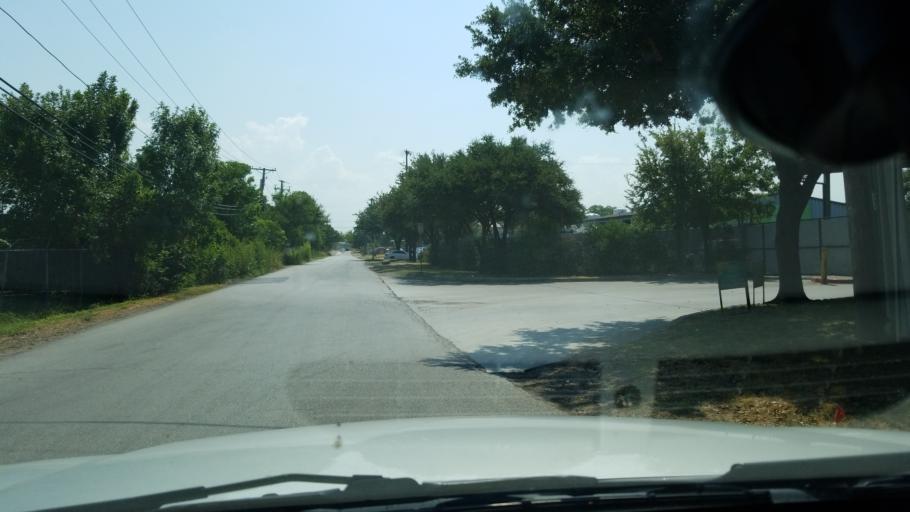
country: US
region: Texas
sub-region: Dallas County
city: Farmers Branch
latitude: 32.8666
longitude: -96.9119
